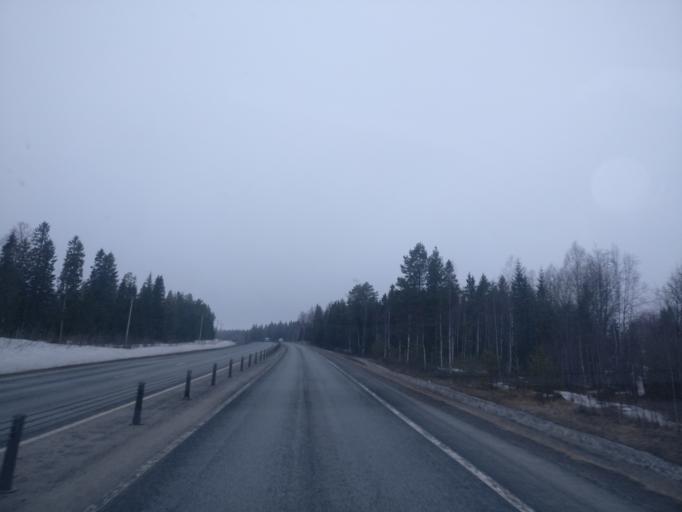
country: FI
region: Lapland
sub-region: Kemi-Tornio
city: Simo
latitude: 65.6685
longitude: 24.9648
